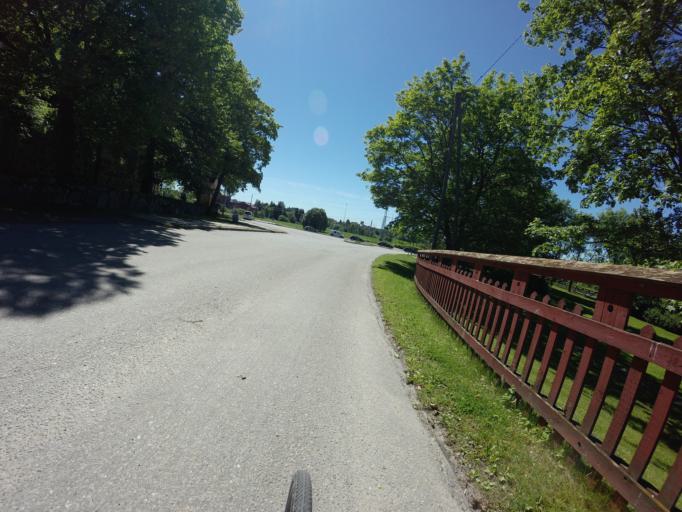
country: FI
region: Varsinais-Suomi
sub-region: Turku
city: Turku
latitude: 60.4737
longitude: 22.2928
